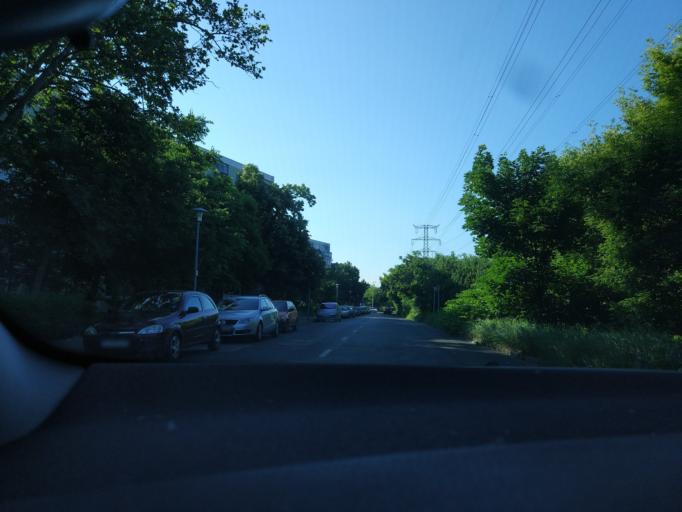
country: HU
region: Budapest
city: Budapest XX. keruelet
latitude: 47.4616
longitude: 19.1115
